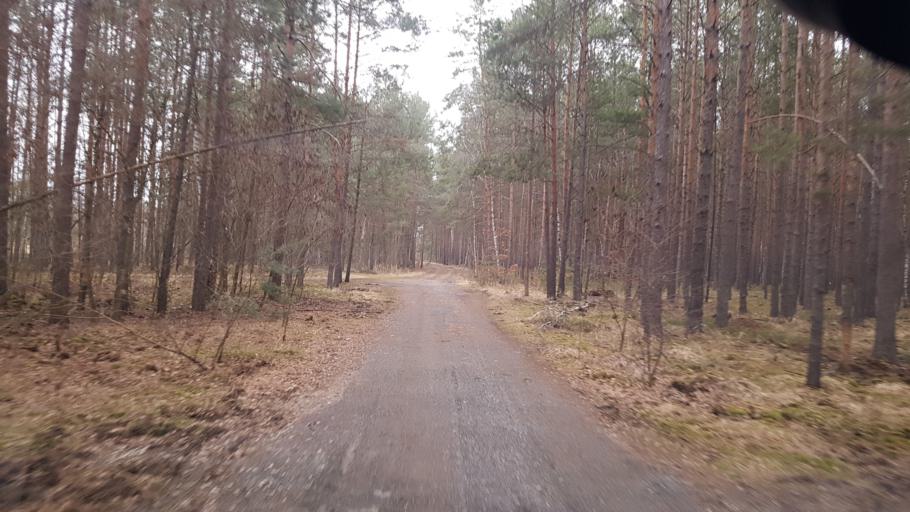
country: DE
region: Brandenburg
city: Trobitz
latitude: 51.6096
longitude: 13.4591
